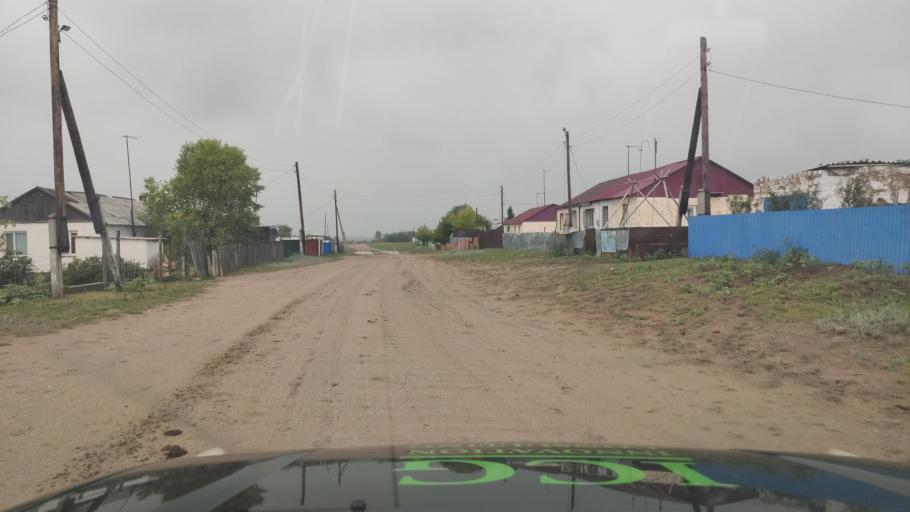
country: KZ
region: Pavlodar
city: Aksu
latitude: 52.0530
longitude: 77.1390
